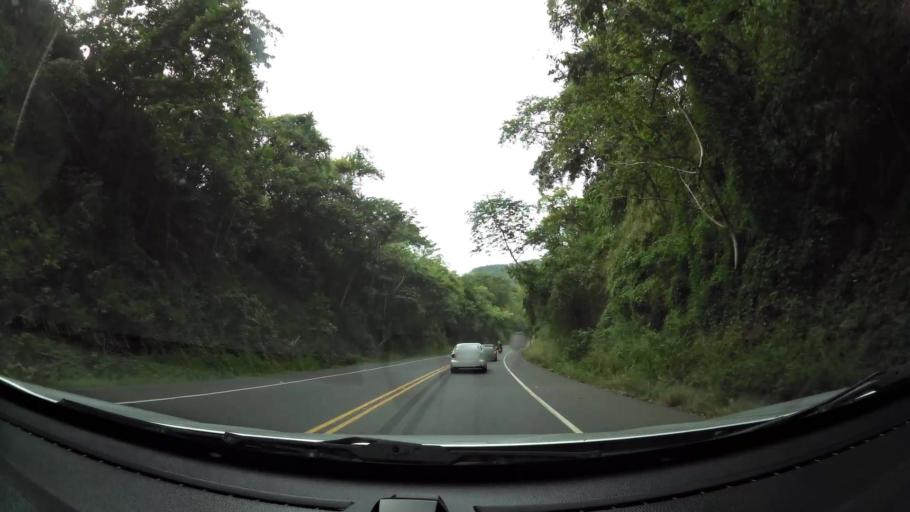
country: CR
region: Puntarenas
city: Esparza
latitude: 9.9091
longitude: -84.6698
